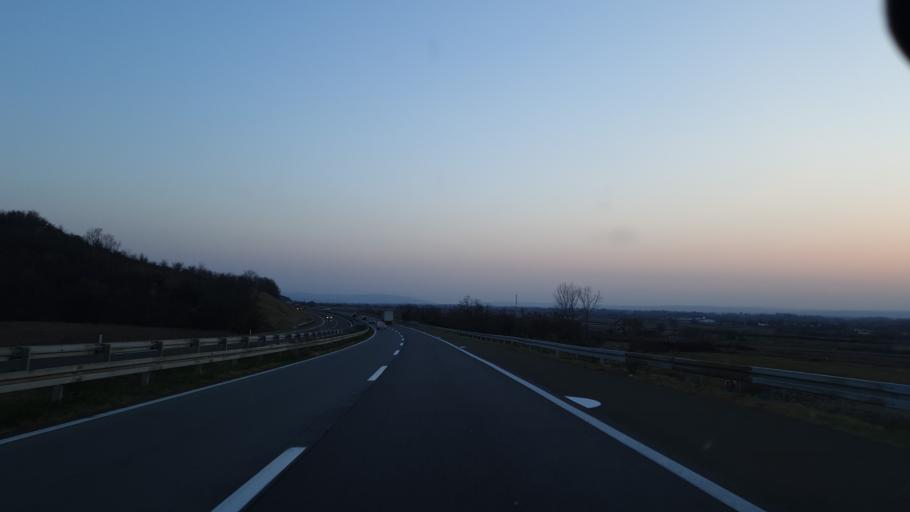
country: RS
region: Central Serbia
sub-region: Pomoravski Okrug
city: Paracin
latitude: 43.8390
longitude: 21.4274
